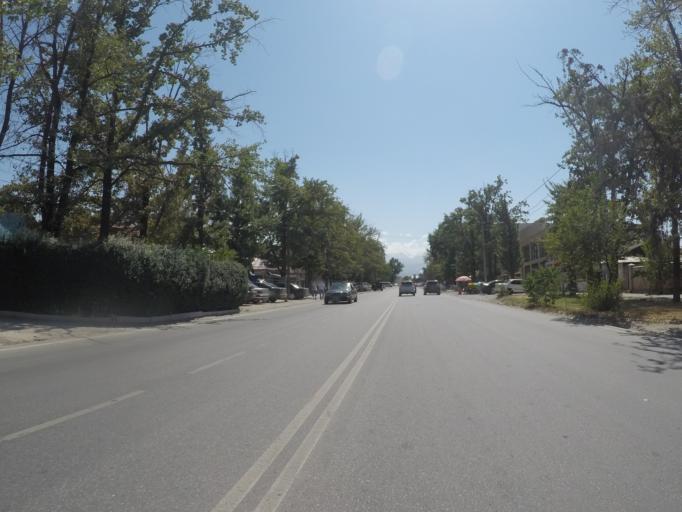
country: KG
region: Chuy
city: Bishkek
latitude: 42.8454
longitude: 74.5769
